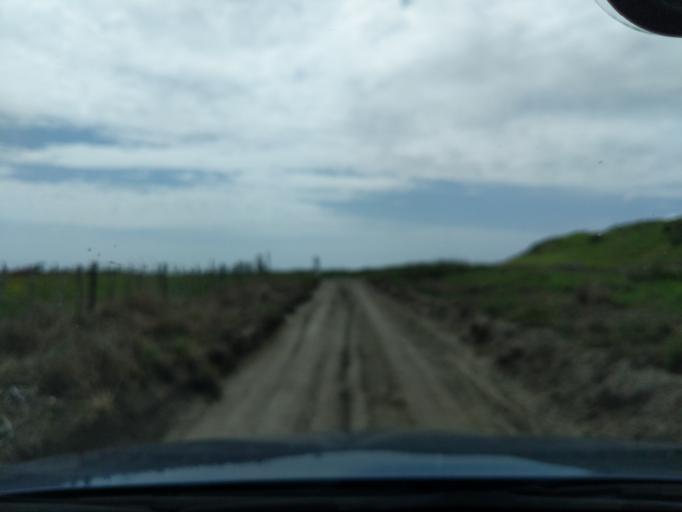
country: NZ
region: Tasman
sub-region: Tasman District
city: Takaka
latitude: -40.6424
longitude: 172.4324
